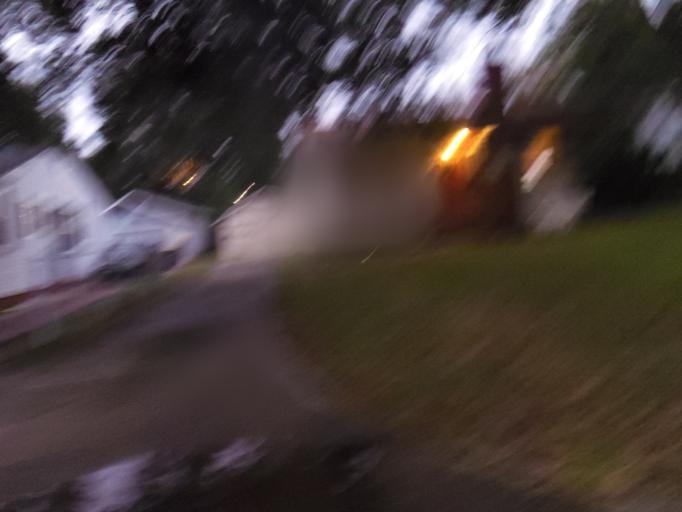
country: US
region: Florida
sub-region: Duval County
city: Jacksonville
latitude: 30.3101
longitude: -81.6558
